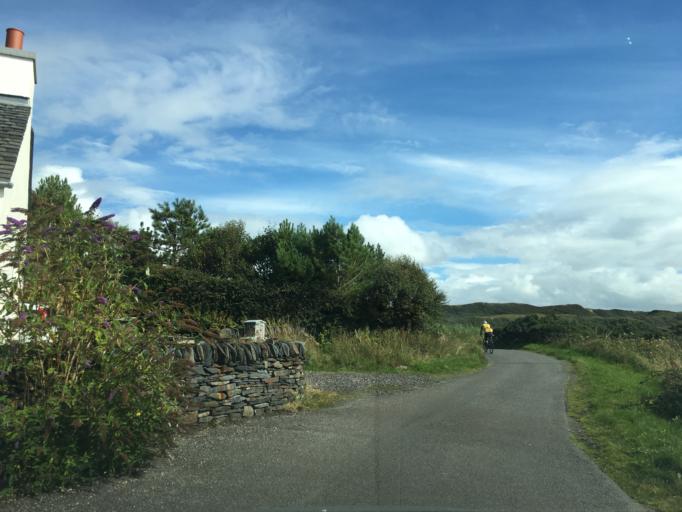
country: GB
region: Scotland
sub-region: Argyll and Bute
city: Isle Of Mull
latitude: 56.2494
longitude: -5.6521
